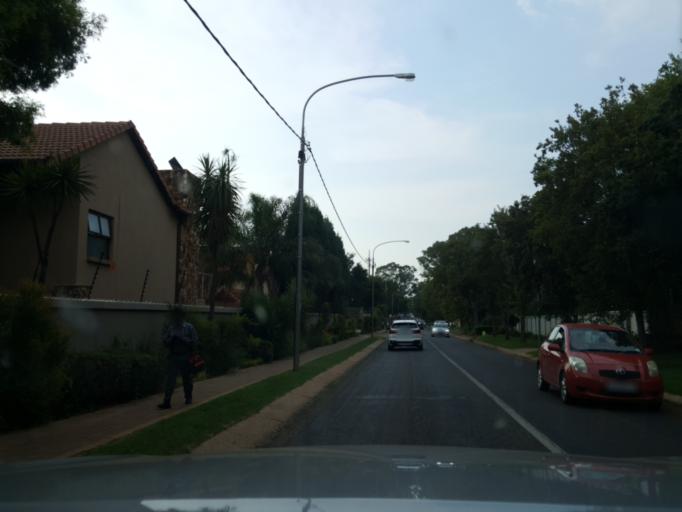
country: ZA
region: Gauteng
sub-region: City of Tshwane Metropolitan Municipality
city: Centurion
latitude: -25.8746
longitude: 28.2131
